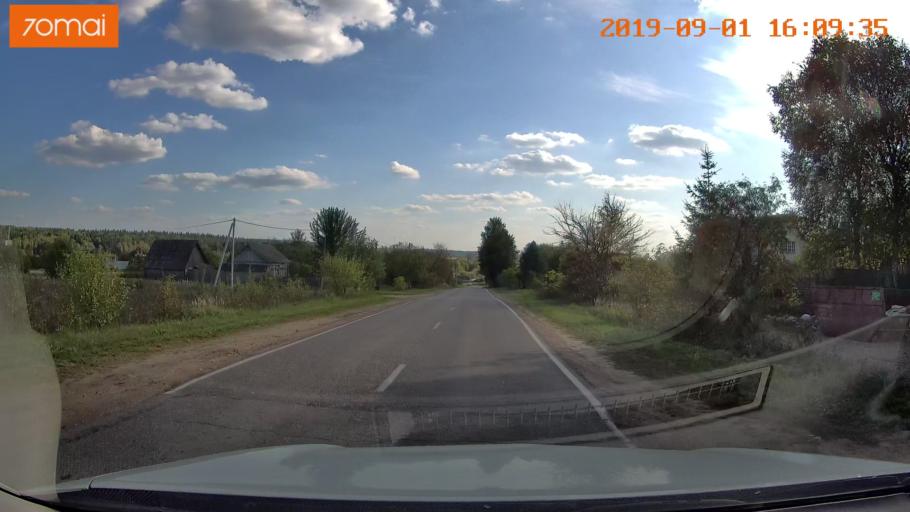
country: RU
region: Kaluga
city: Maloyaroslavets
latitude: 54.9702
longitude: 36.4636
